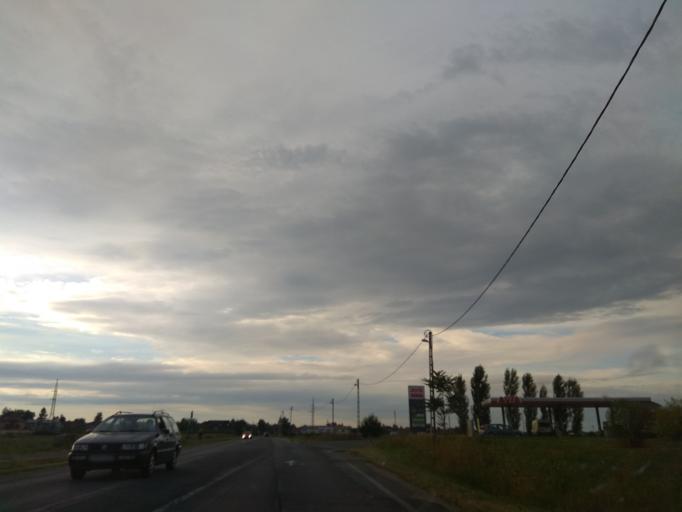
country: HU
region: Borsod-Abauj-Zemplen
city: Miskolc
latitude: 48.0821
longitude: 20.8200
